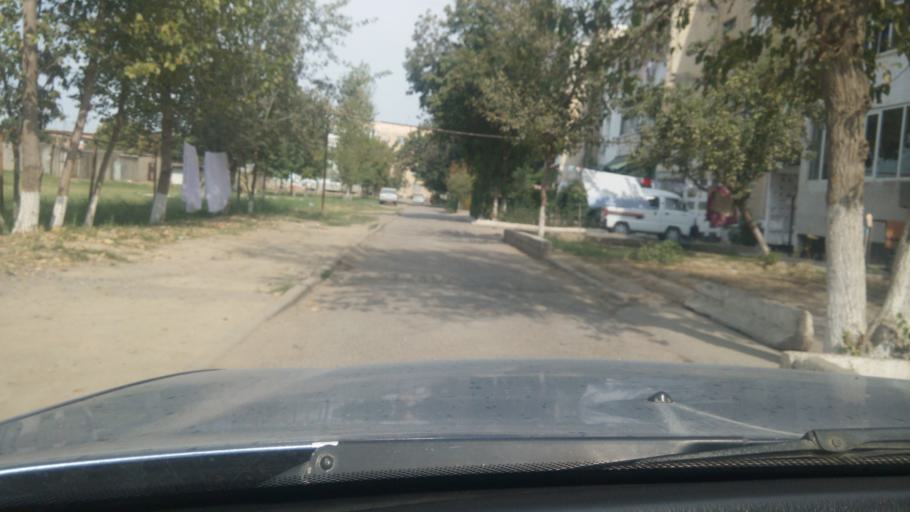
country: UZ
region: Sirdaryo
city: Guliston
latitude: 40.5139
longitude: 68.7814
